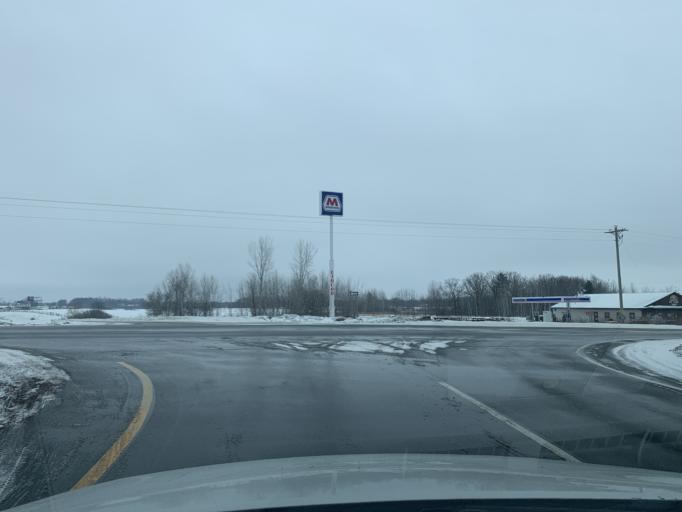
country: US
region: Minnesota
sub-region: Pine County
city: Rock Creek
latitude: 45.7665
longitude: -92.9884
